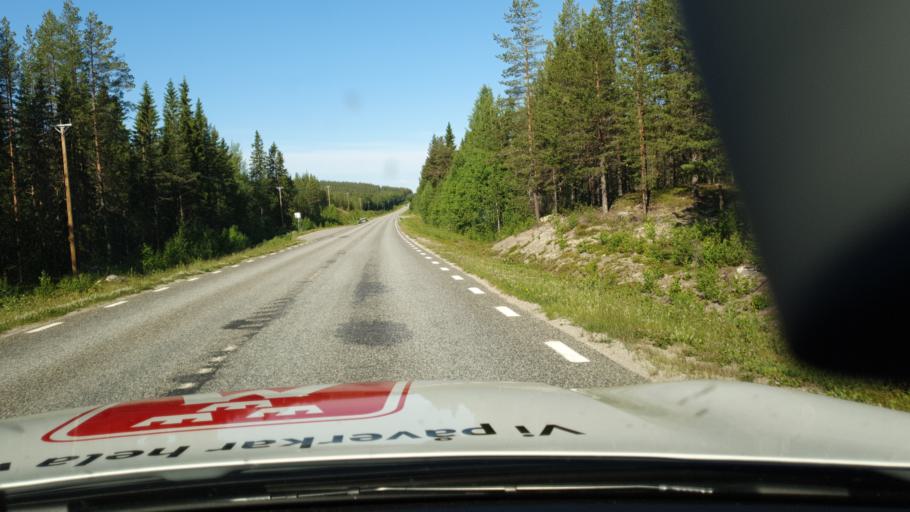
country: SE
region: Vaesterbotten
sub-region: Lycksele Kommun
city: Lycksele
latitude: 64.5669
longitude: 18.6004
